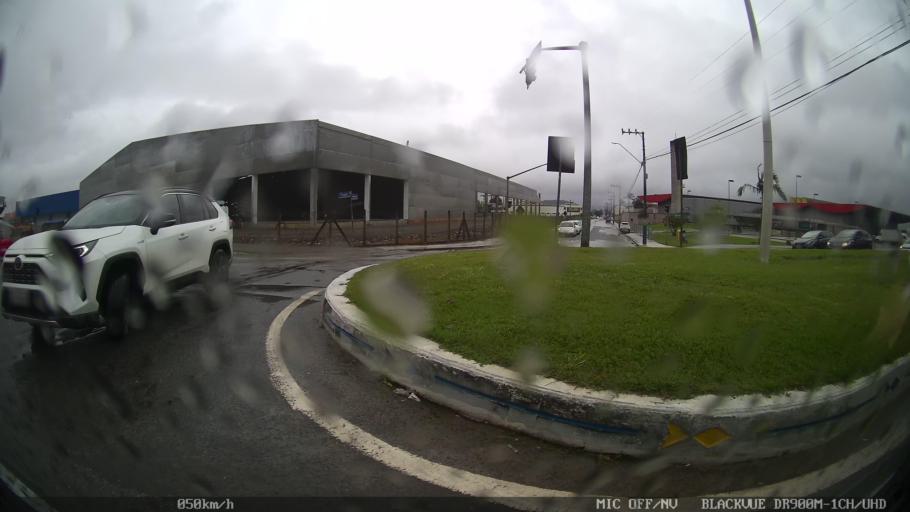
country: BR
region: Santa Catarina
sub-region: Itajai
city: Itajai
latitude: -26.9134
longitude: -48.6937
